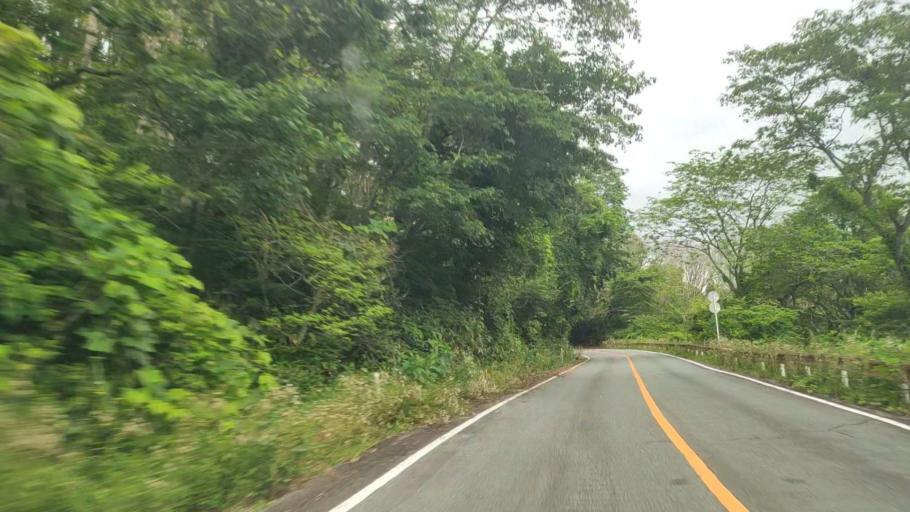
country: JP
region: Tottori
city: Kurayoshi
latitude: 35.3024
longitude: 133.6231
